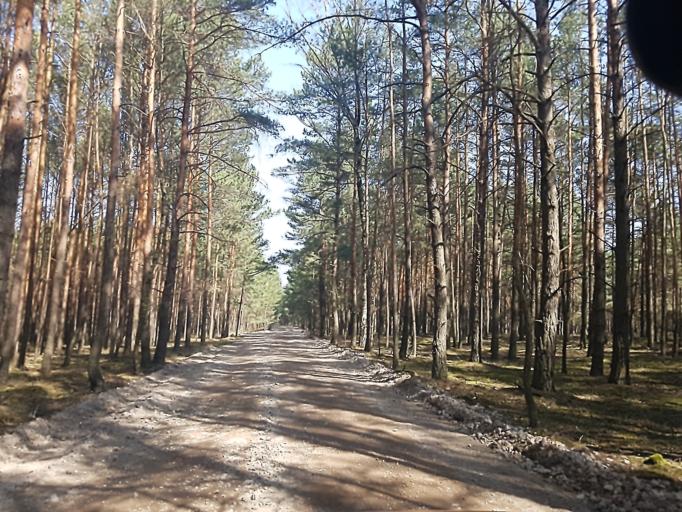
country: DE
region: Brandenburg
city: Tschernitz
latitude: 51.6616
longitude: 14.5637
